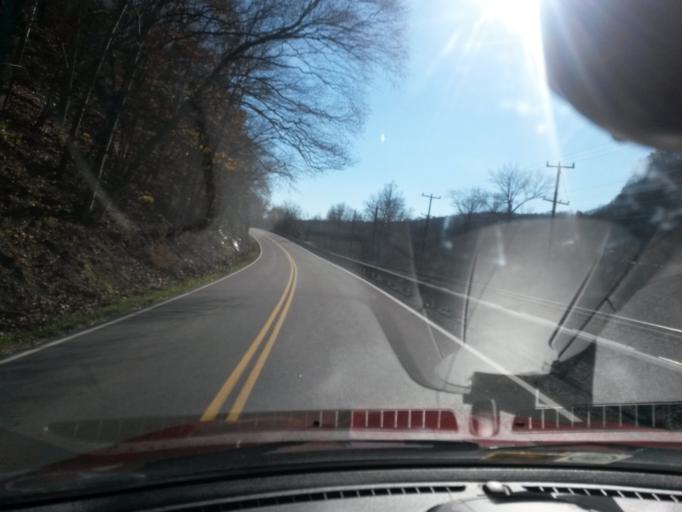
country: US
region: Virginia
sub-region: Botetourt County
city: Fincastle
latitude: 37.6439
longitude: -79.8070
